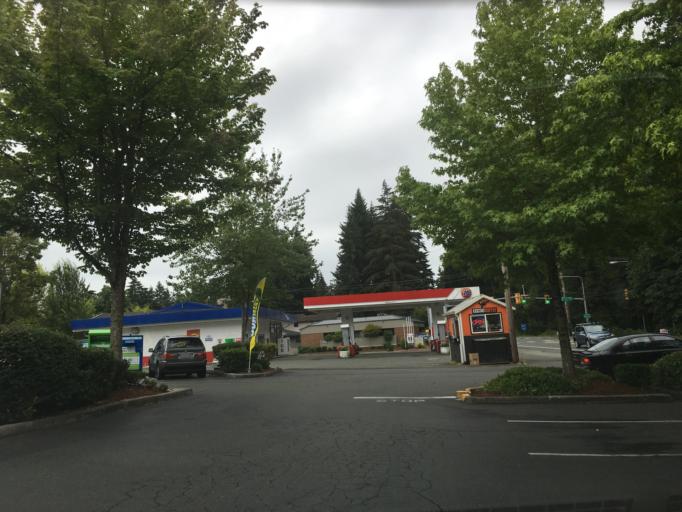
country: US
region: Washington
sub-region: King County
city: Inglewood-Finn Hill
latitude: 47.7288
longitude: -122.2441
